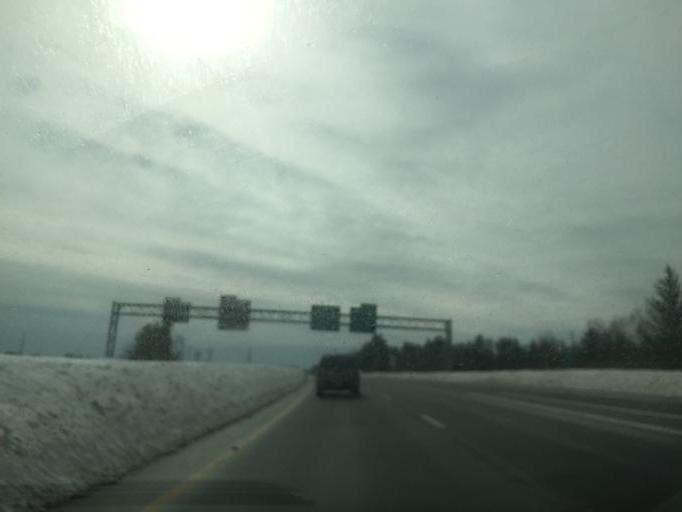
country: US
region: New Hampshire
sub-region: Strafford County
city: Rochester
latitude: 43.3147
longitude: -70.9967
